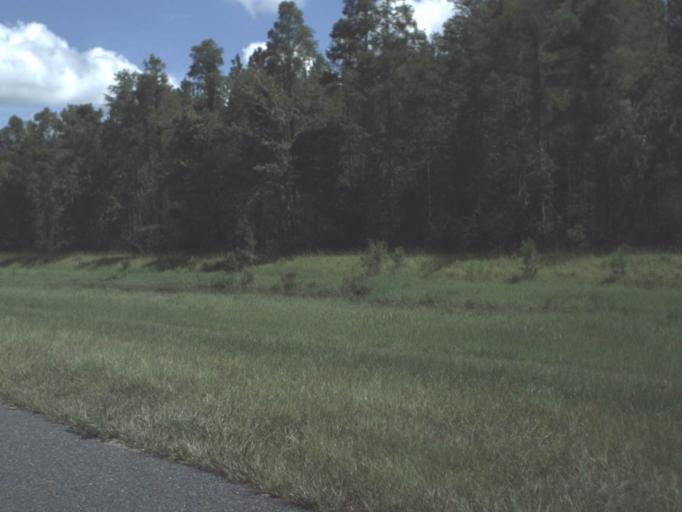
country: US
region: Florida
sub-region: Levy County
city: Chiefland
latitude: 29.3537
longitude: -82.7844
